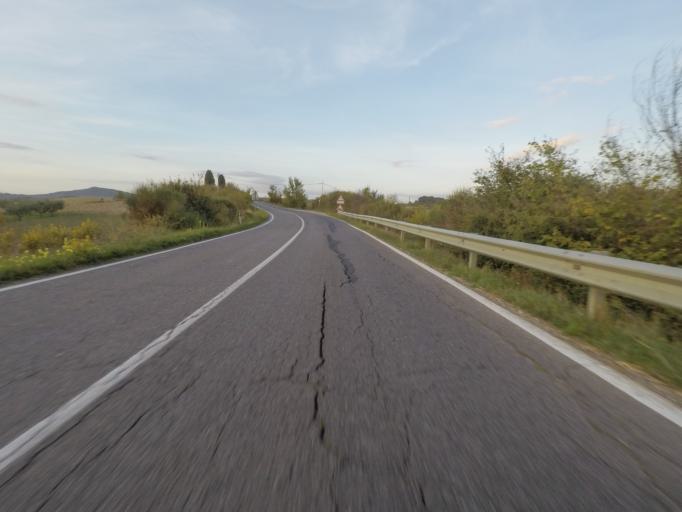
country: IT
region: Tuscany
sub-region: Provincia di Siena
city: Pienza
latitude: 43.0932
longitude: 11.6888
